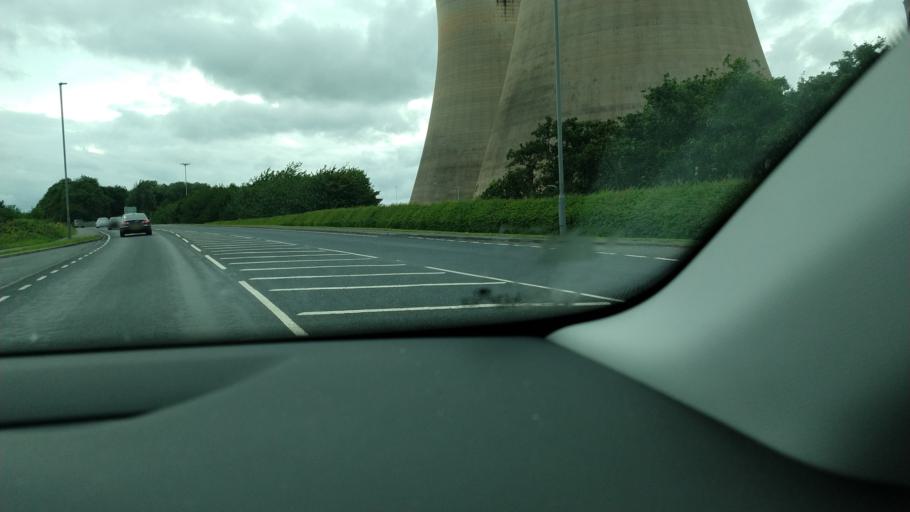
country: GB
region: England
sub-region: North Yorkshire
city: Camblesforth
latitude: 53.7298
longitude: -0.9948
